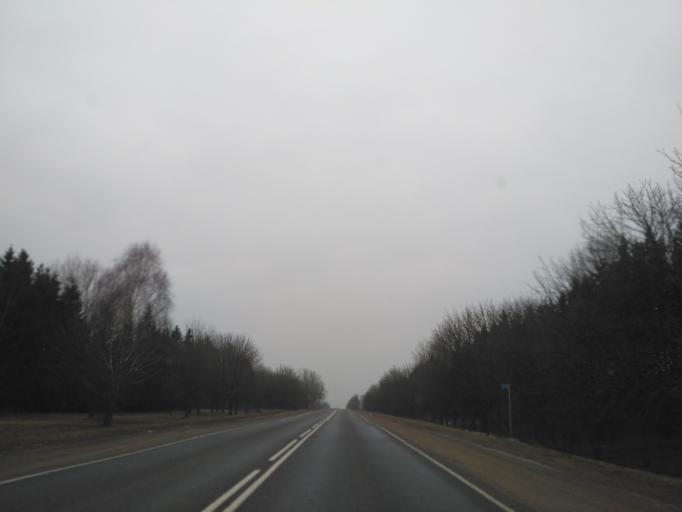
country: BY
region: Minsk
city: Haradzyeya
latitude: 53.3815
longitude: 26.5573
